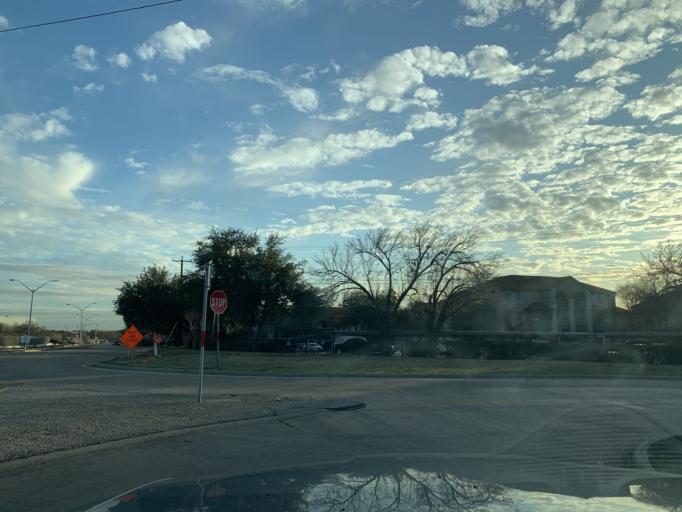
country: US
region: Texas
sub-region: Tarrant County
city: Euless
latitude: 32.8347
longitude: -97.0697
